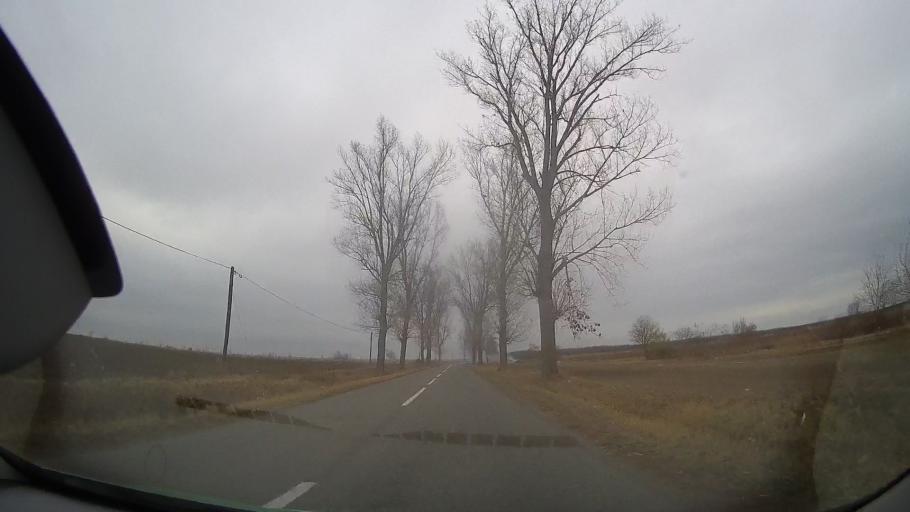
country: RO
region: Braila
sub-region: Comuna Rosiori
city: Rosiori
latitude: 44.8165
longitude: 27.3931
